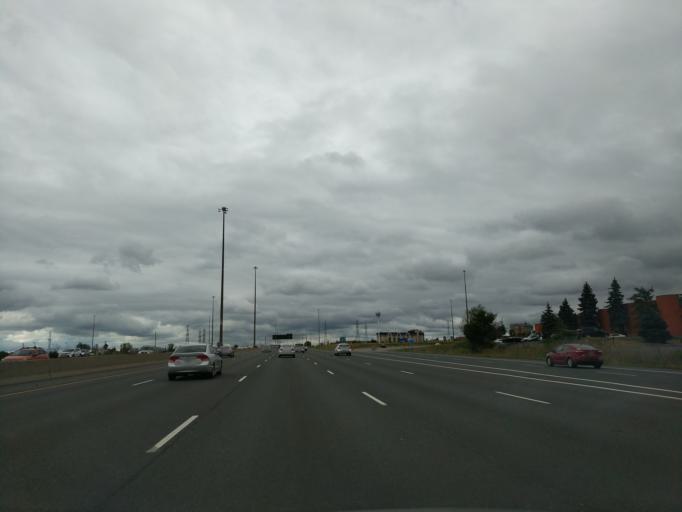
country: CA
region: Ontario
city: Concord
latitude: 43.7507
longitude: -79.5301
